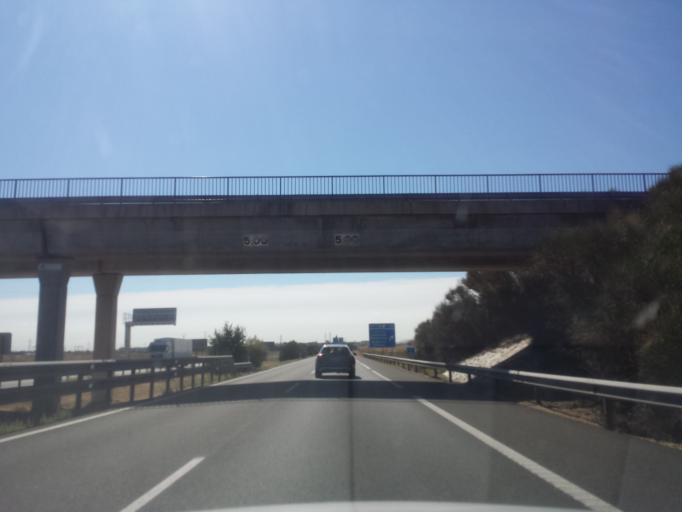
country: ES
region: Castille and Leon
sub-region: Provincia de Valladolid
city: Tordesillas
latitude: 41.5171
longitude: -5.0294
